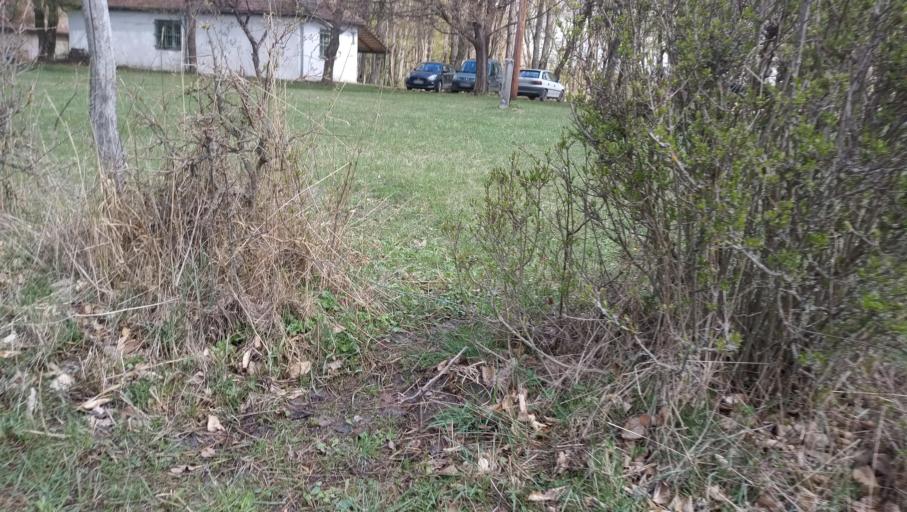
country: HU
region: Veszprem
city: Herend
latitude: 47.2062
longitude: 17.7596
